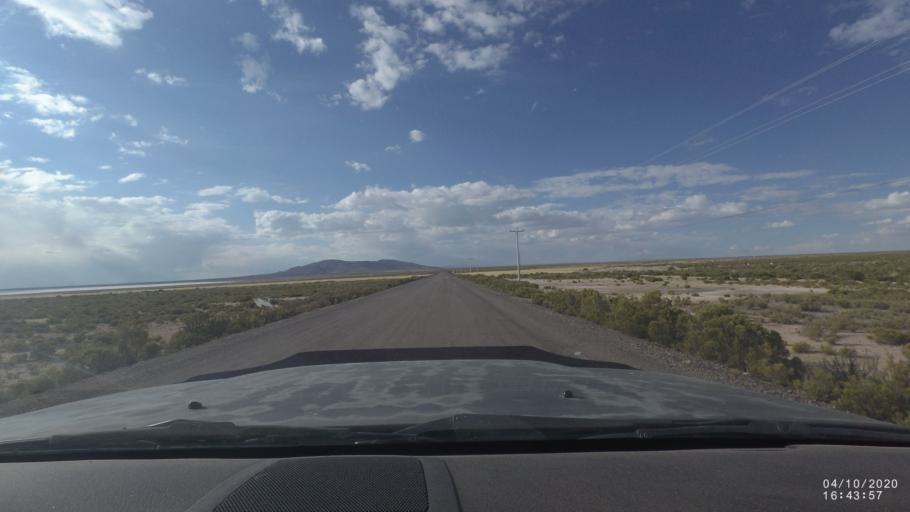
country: BO
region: Oruro
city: Poopo
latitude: -18.6900
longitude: -67.5578
